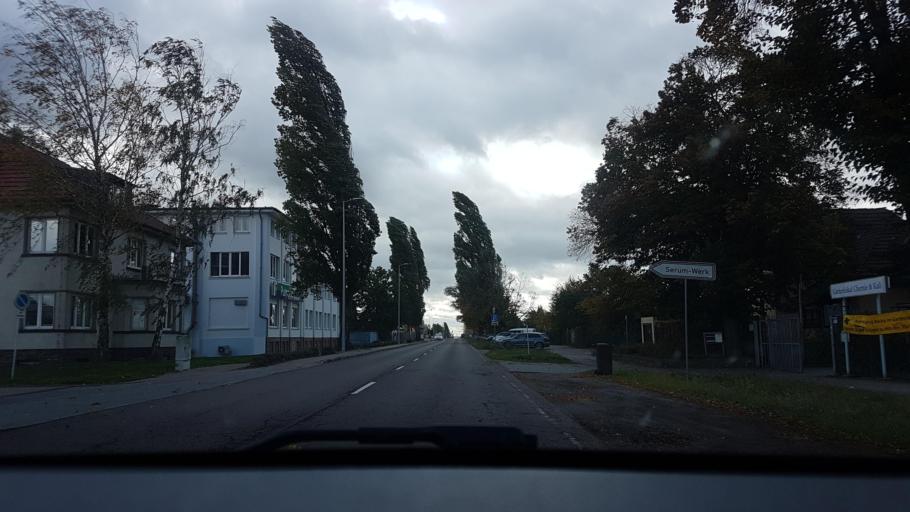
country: DE
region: Saxony-Anhalt
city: Bernburg
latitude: 51.7817
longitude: 11.7453
